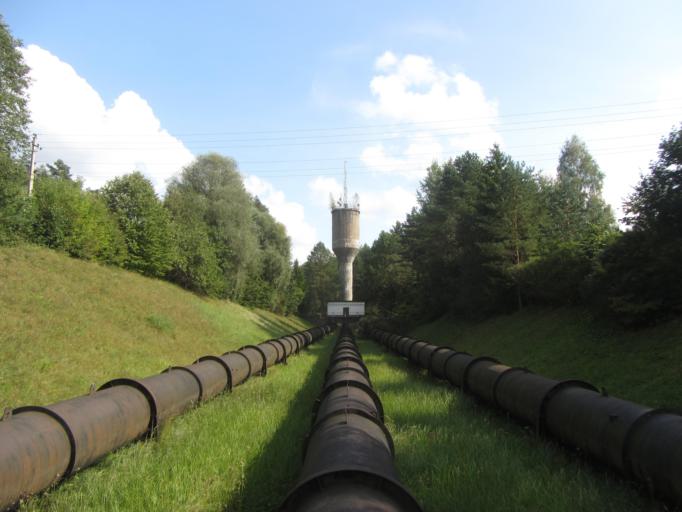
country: LT
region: Utenos apskritis
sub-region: Utena
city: Utena
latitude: 55.6568
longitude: 25.8763
